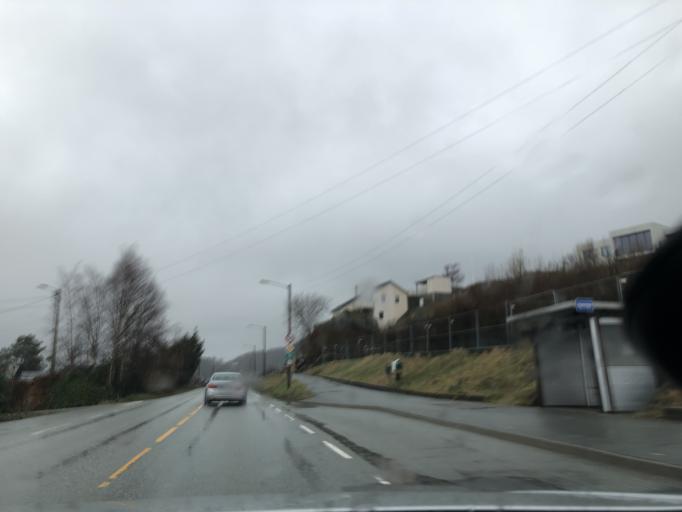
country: NO
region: Rogaland
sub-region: Strand
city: Tau
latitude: 59.0555
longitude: 5.9187
